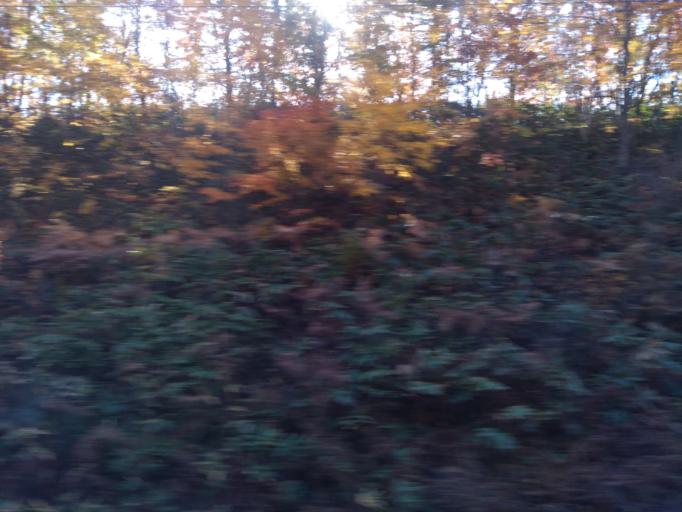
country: JP
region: Hokkaido
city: Kitahiroshima
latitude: 42.9955
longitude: 141.5390
